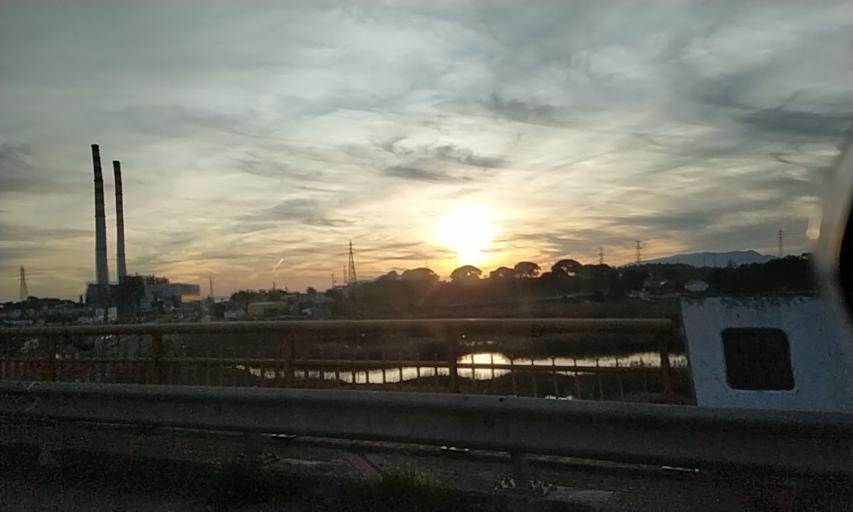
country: PT
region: Setubal
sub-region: Setubal
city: Setubal
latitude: 38.5173
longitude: -8.8391
